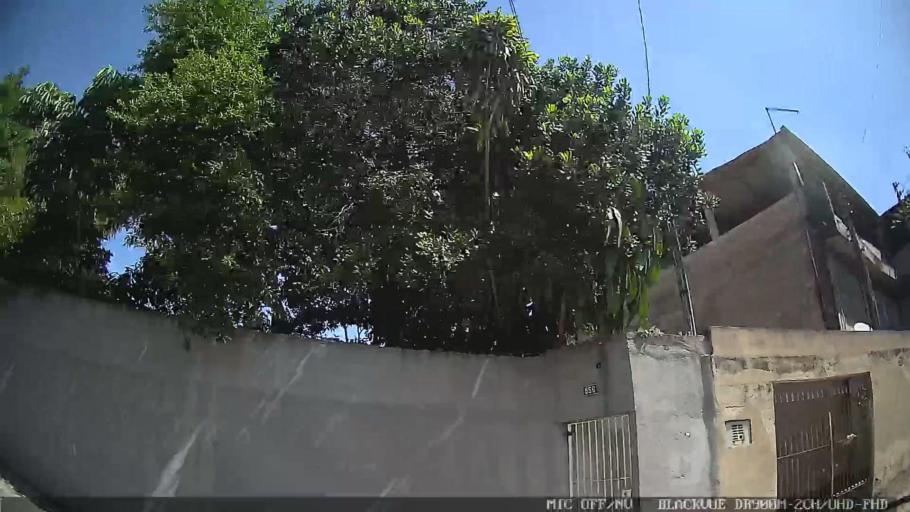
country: BR
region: Sao Paulo
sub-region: Sao Caetano Do Sul
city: Sao Caetano do Sul
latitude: -23.5800
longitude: -46.5043
